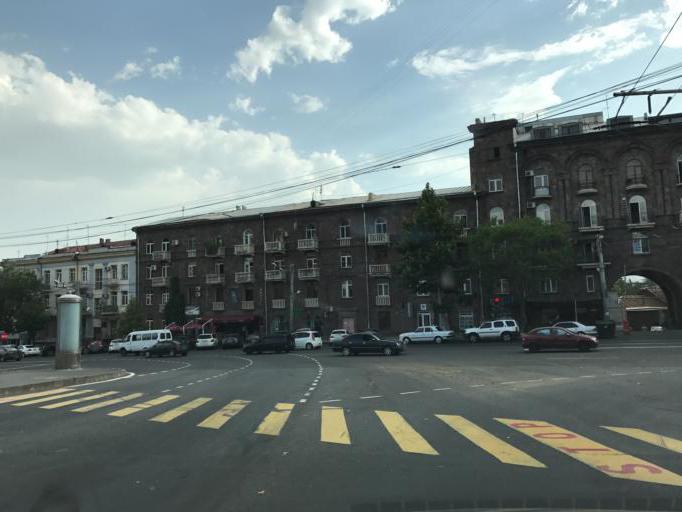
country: AM
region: Yerevan
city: Yerevan
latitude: 40.1870
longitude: 44.5259
